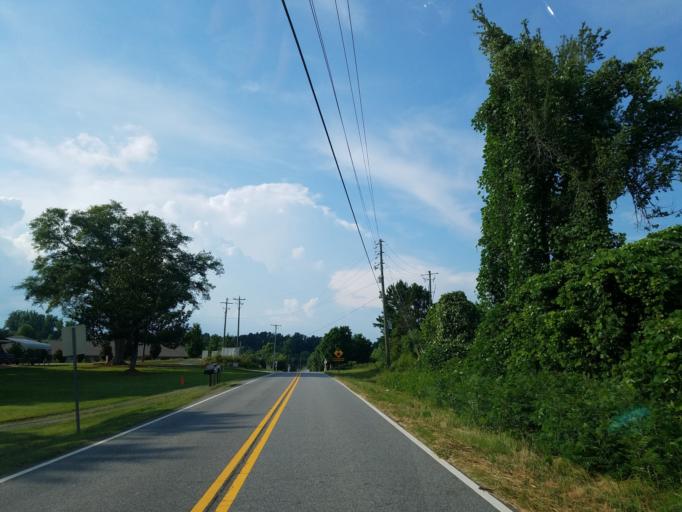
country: US
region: Georgia
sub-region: Forsyth County
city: Cumming
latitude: 34.3009
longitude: -84.0667
